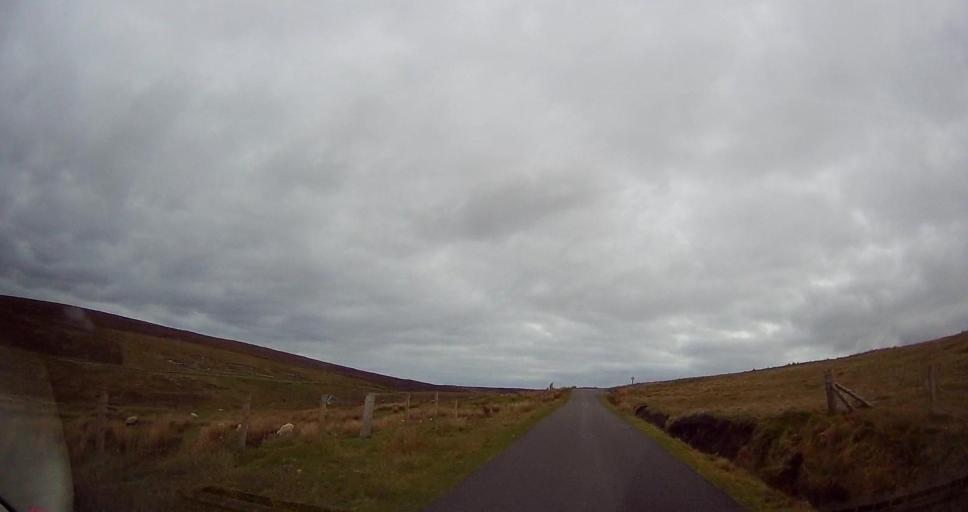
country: GB
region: Scotland
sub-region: Shetland Islands
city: Shetland
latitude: 60.5923
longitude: -1.0709
